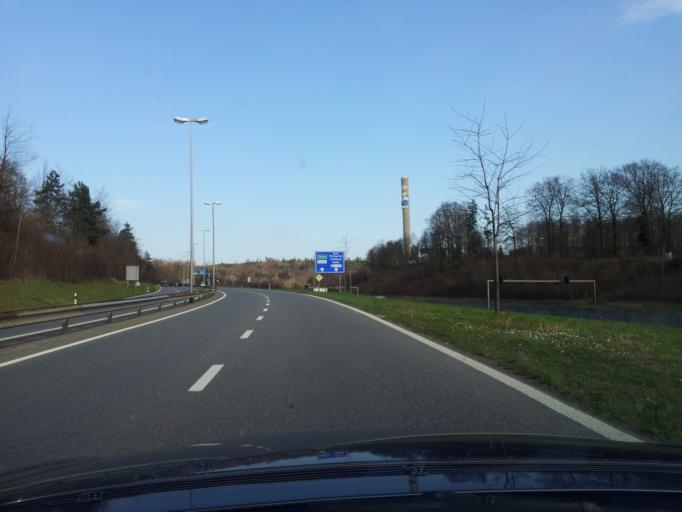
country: CH
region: Aargau
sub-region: Bezirk Baden
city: Birmenstorf
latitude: 47.4573
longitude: 8.2742
